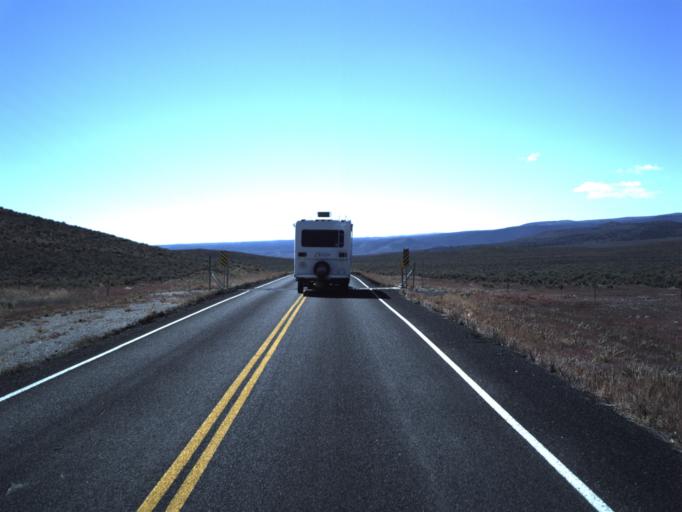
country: US
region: Utah
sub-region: Piute County
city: Junction
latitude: 38.2308
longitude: -111.9952
